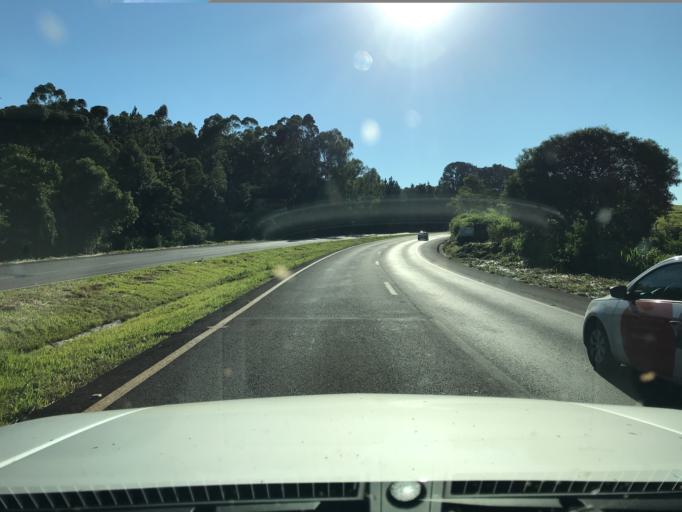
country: BR
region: Parana
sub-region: Cascavel
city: Cascavel
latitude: -24.8928
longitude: -53.5397
